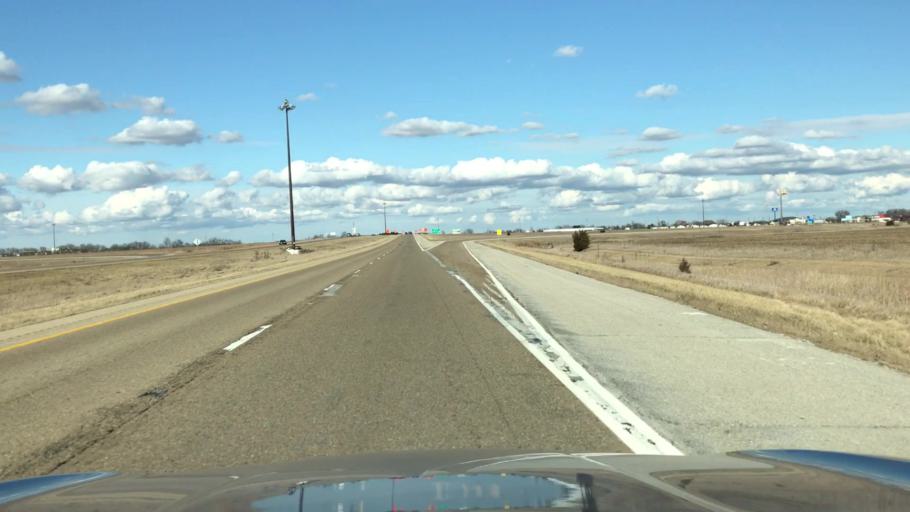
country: US
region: Illinois
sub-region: McLean County
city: Chenoa
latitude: 40.7351
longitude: -88.7372
